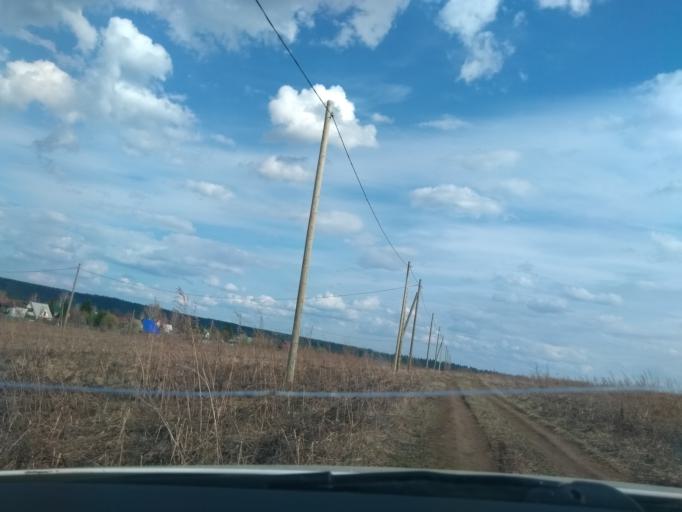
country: RU
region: Perm
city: Sylva
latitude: 57.8440
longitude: 56.7887
